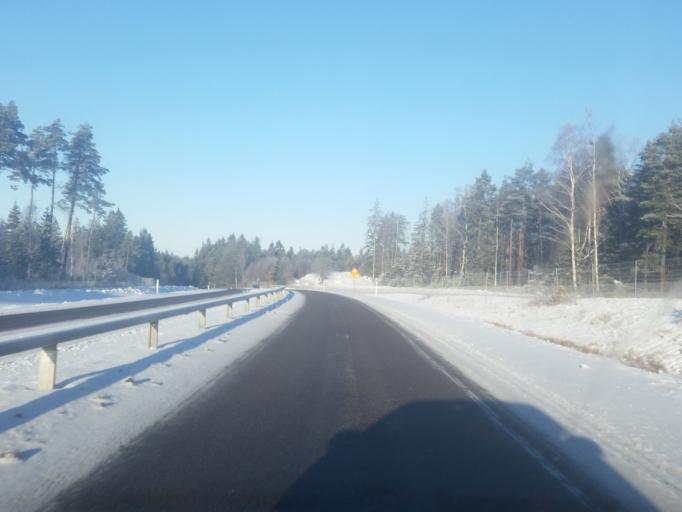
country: SE
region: Vaestra Goetaland
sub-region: Partille Kommun
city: Furulund
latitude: 57.6895
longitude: 12.1644
